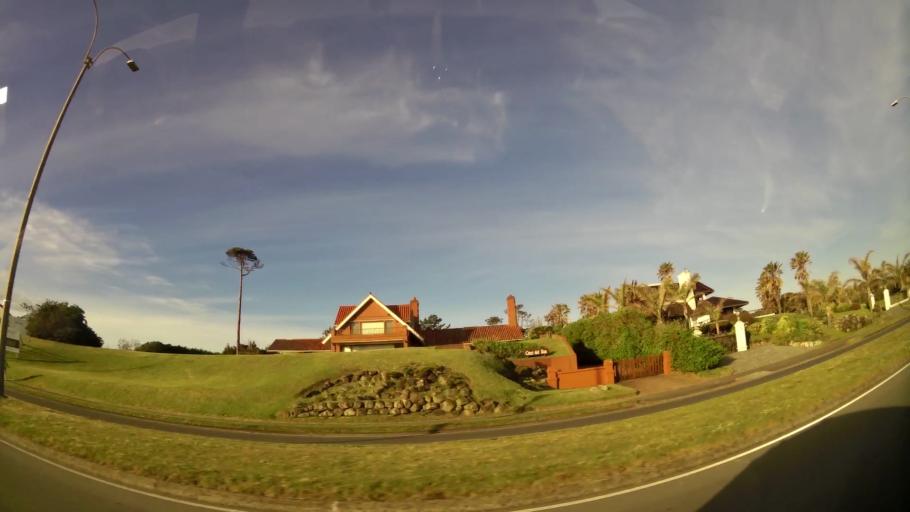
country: UY
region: Maldonado
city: Maldonado
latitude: -34.9148
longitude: -54.9816
